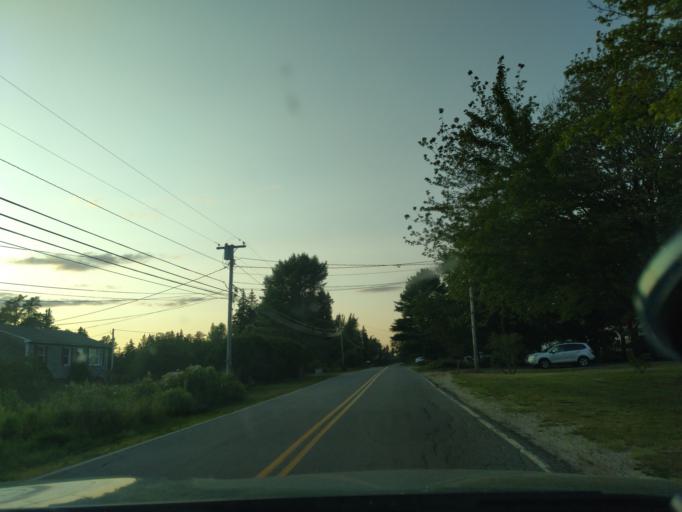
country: US
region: Maine
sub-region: Hancock County
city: Gouldsboro
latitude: 44.3744
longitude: -68.0349
